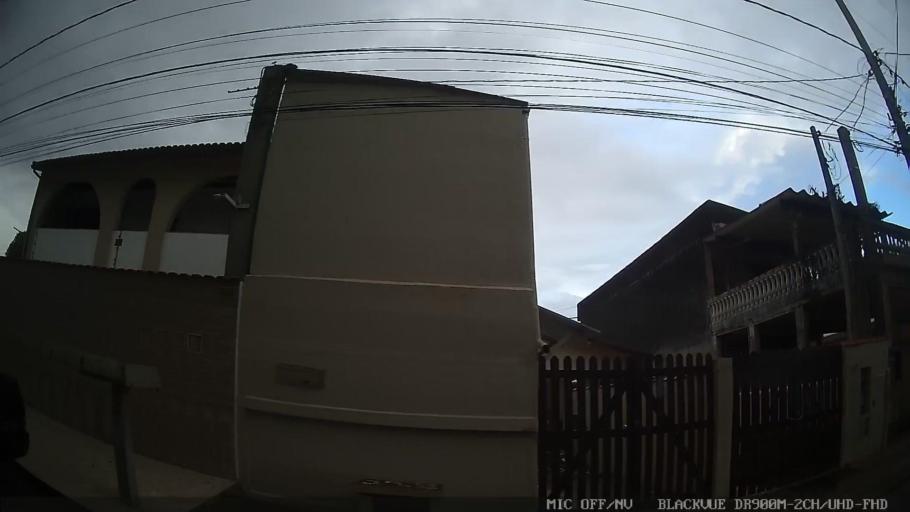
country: BR
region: Sao Paulo
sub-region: Itanhaem
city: Itanhaem
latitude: -24.1802
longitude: -46.7944
